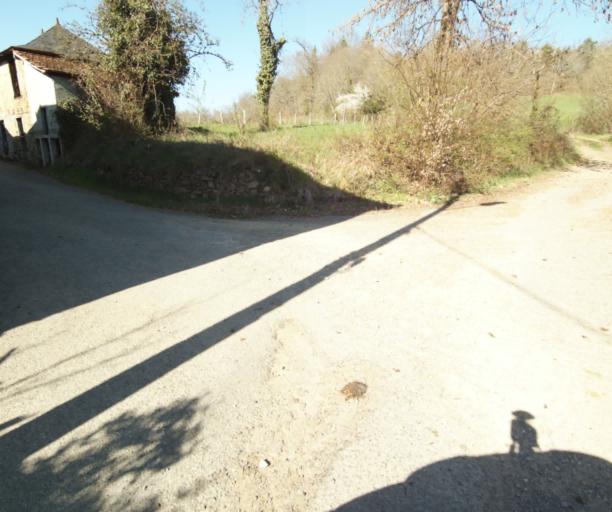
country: FR
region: Limousin
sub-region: Departement de la Correze
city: Tulle
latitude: 45.2901
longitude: 1.7322
